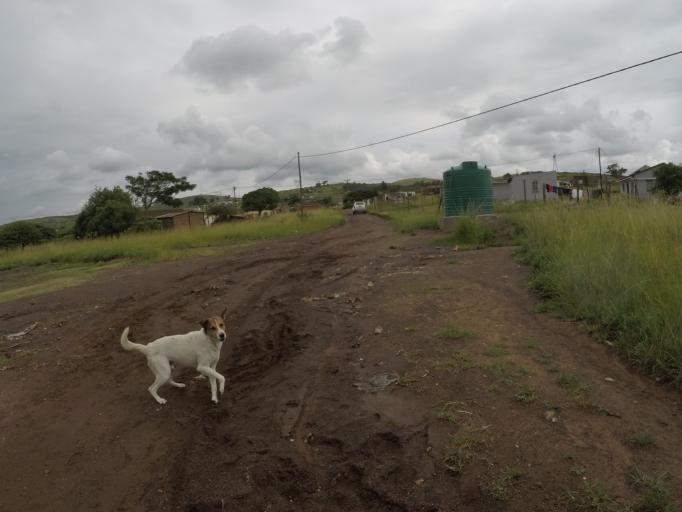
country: ZA
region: KwaZulu-Natal
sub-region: uThungulu District Municipality
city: Empangeni
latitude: -28.7128
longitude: 31.8557
